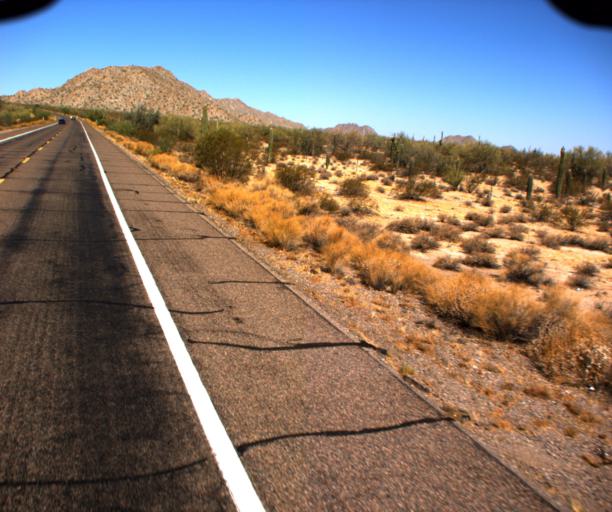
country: US
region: Arizona
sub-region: Pinal County
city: Blackwater
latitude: 33.0174
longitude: -111.6630
